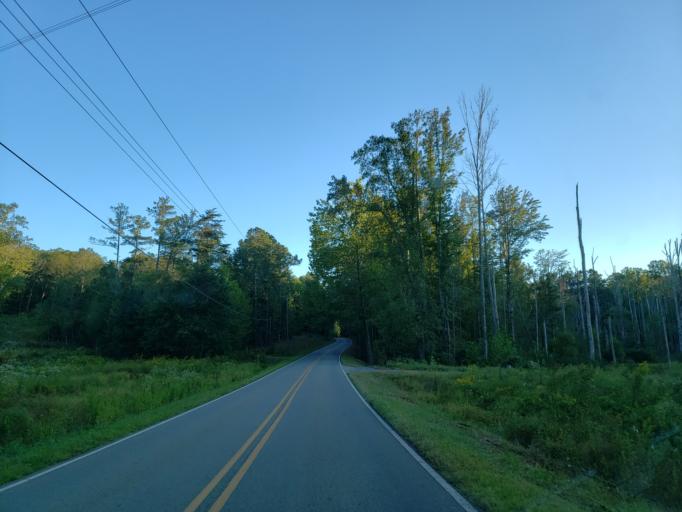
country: US
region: Georgia
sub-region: Bartow County
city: Rydal
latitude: 34.3794
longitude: -84.5894
